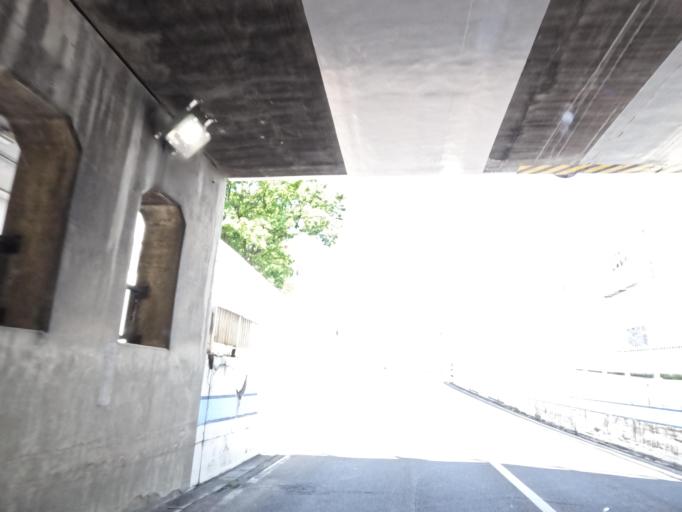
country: JP
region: Hokkaido
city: Takikawa
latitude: 43.5592
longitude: 141.9029
